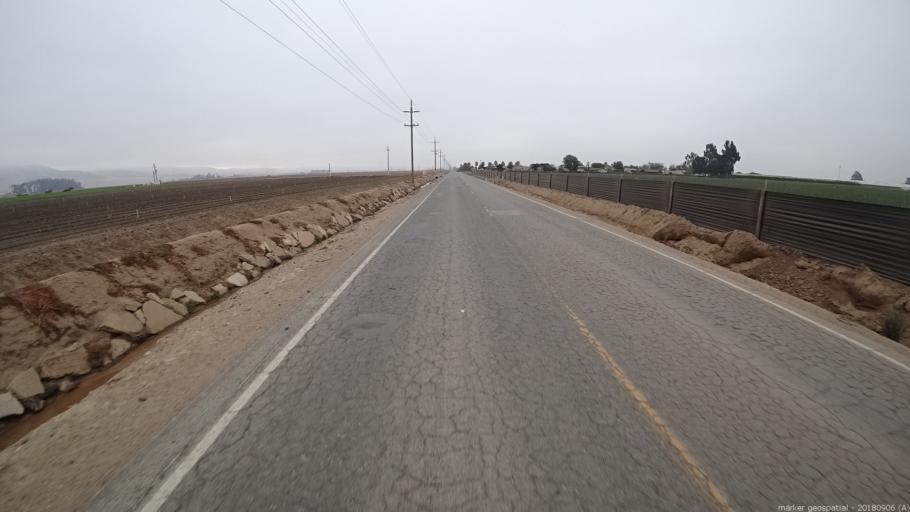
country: US
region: California
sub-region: Monterey County
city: Chualar
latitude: 36.6338
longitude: -121.5513
